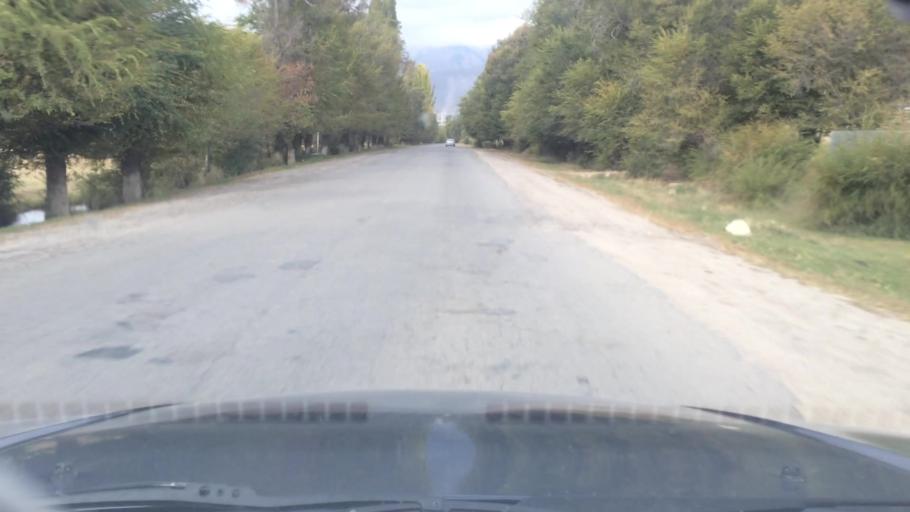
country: KG
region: Ysyk-Koel
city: Tyup
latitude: 42.7828
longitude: 78.2812
